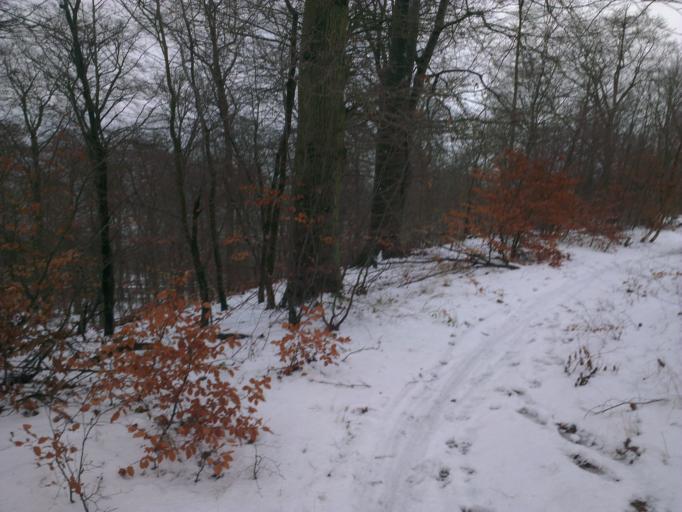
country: DK
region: Capital Region
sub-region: Frederikssund Kommune
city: Jaegerspris
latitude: 55.8521
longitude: 12.0171
